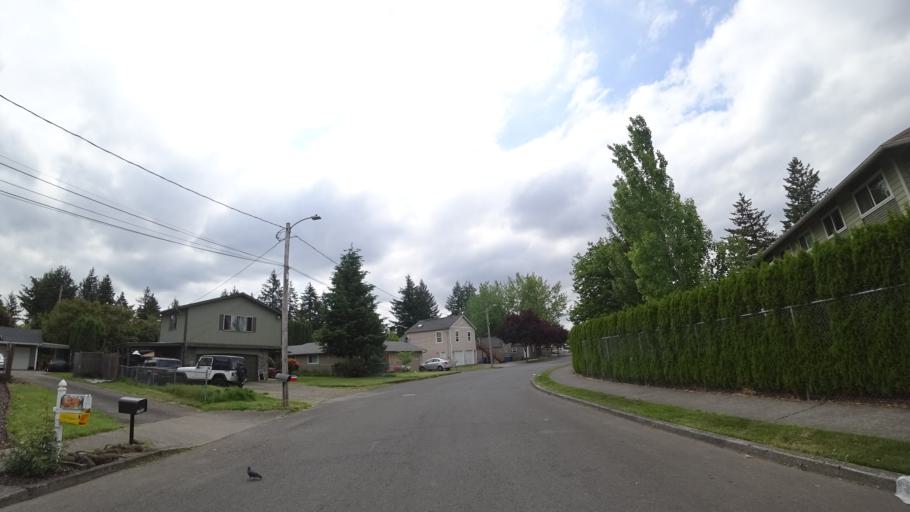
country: US
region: Oregon
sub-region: Multnomah County
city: Fairview
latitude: 45.5178
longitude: -122.4835
